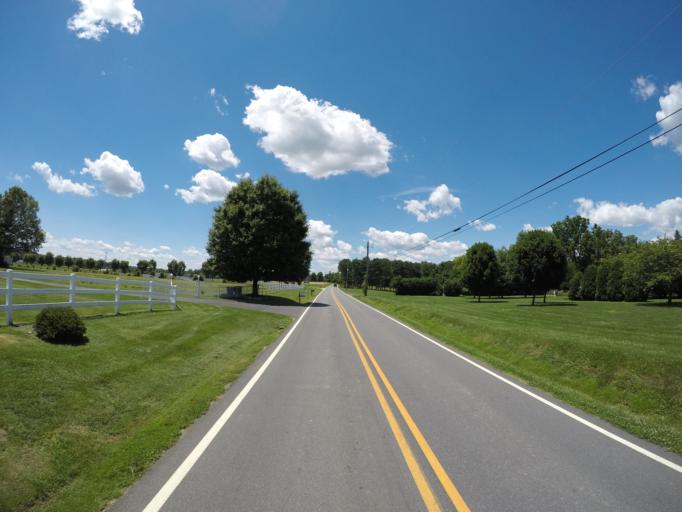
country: US
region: Delaware
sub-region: New Castle County
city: Middletown
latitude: 39.4643
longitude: -75.7641
